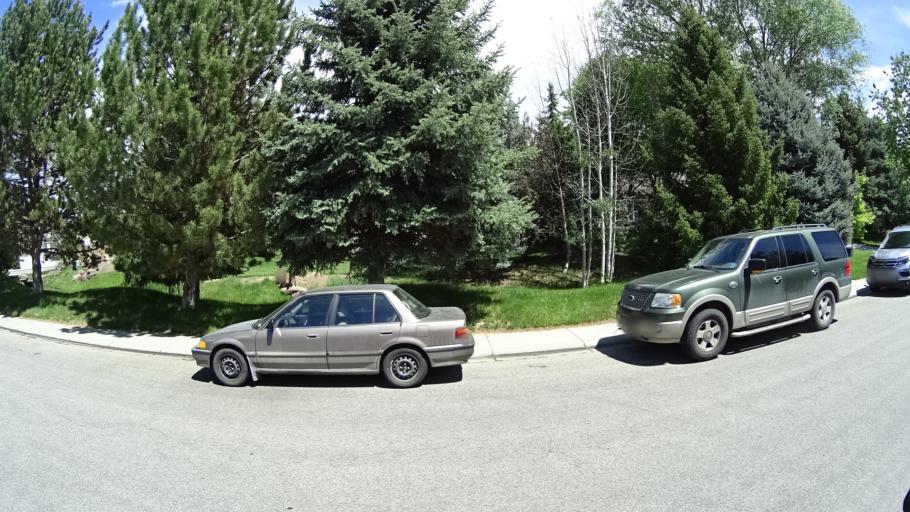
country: US
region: Idaho
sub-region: Ada County
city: Meridian
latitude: 43.5737
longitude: -116.3256
